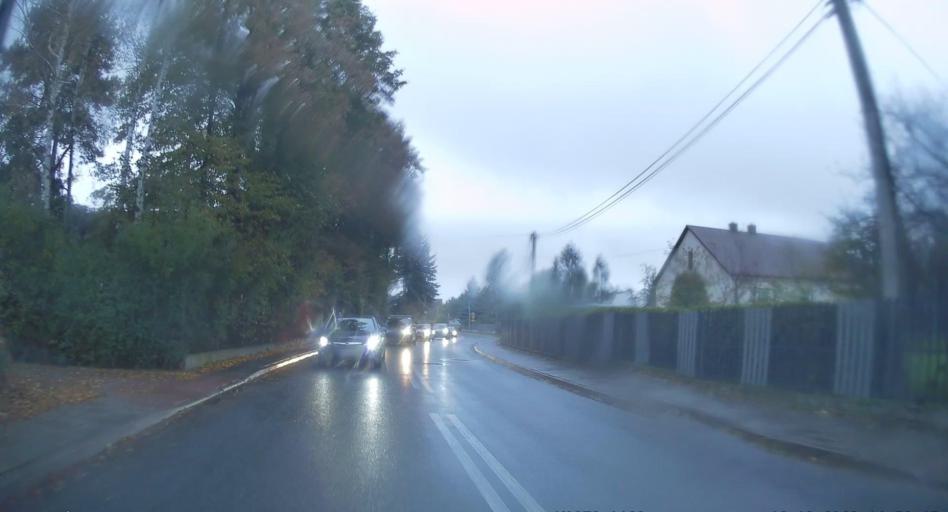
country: PL
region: Lesser Poland Voivodeship
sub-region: Powiat krakowski
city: Ochojno
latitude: 49.9807
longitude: 19.9897
